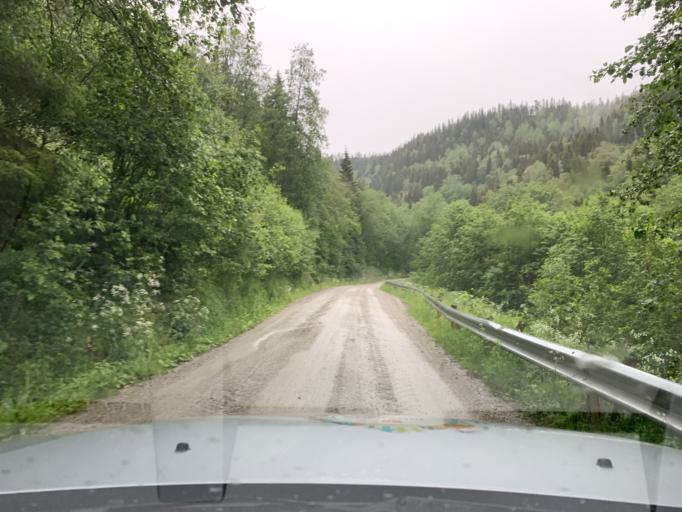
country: NO
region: Oppland
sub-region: Oyer
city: Tretten
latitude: 61.3921
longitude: 10.2726
